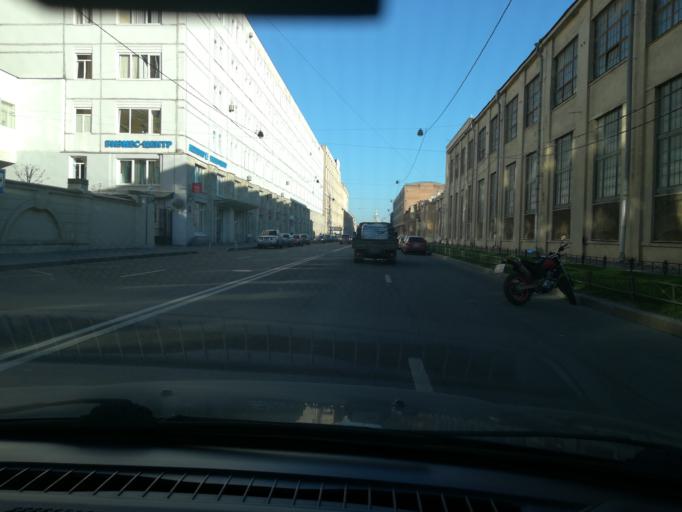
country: RU
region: St.-Petersburg
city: Vasyl'evsky Ostrov
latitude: 59.9320
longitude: 30.2639
